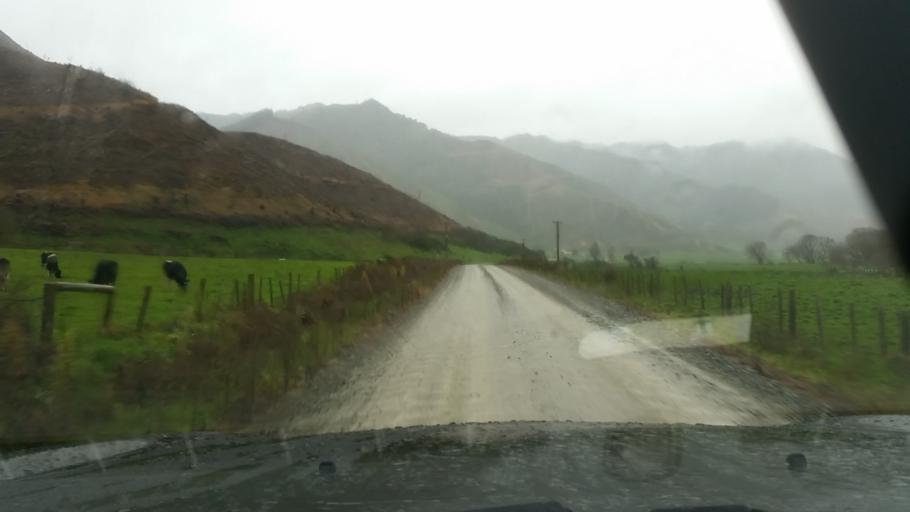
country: NZ
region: Marlborough
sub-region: Marlborough District
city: Picton
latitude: -41.3486
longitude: 173.9296
